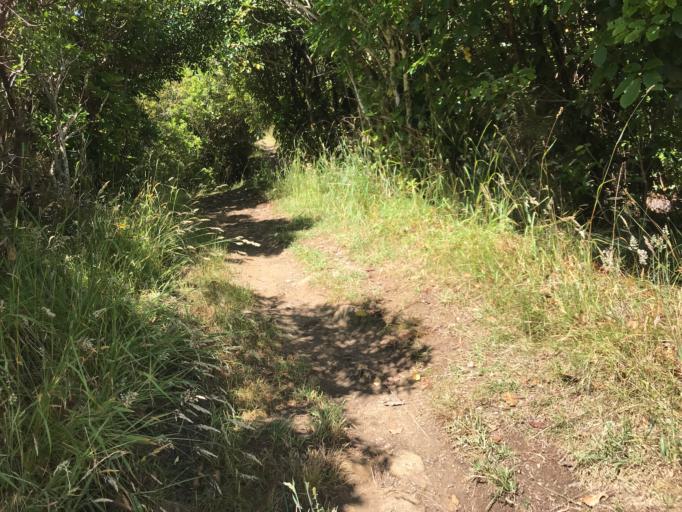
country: NZ
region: Marlborough
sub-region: Marlborough District
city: Picton
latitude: -41.2059
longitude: 174.0241
